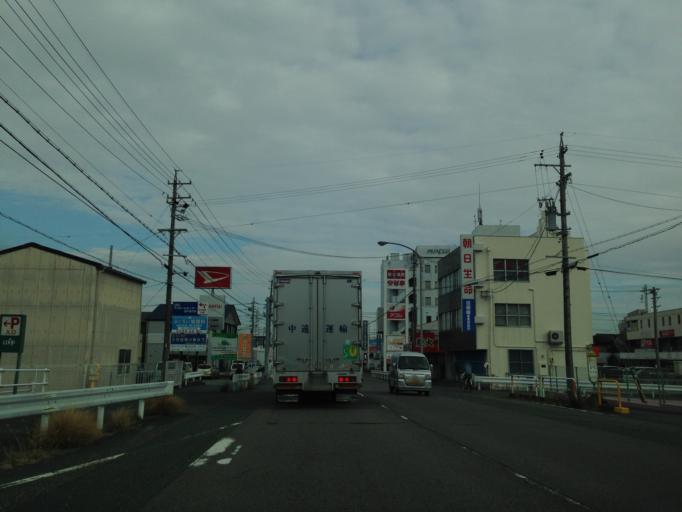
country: JP
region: Shizuoka
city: Fukuroi
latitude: 34.7495
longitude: 137.9202
